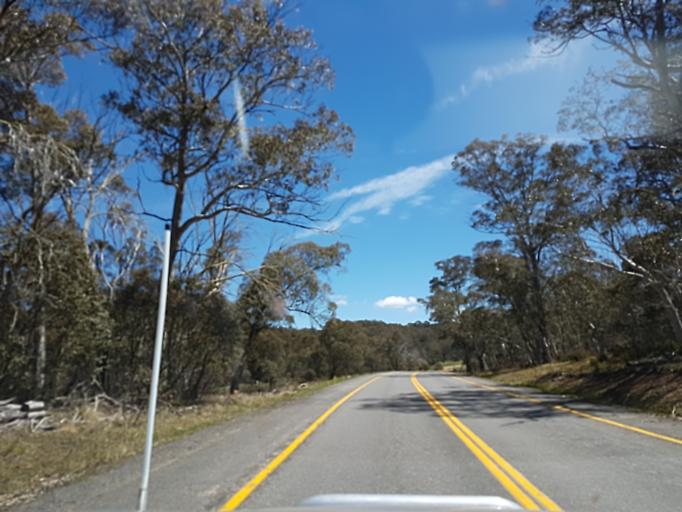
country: AU
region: Victoria
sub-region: Alpine
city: Mount Beauty
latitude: -37.0486
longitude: 147.3176
